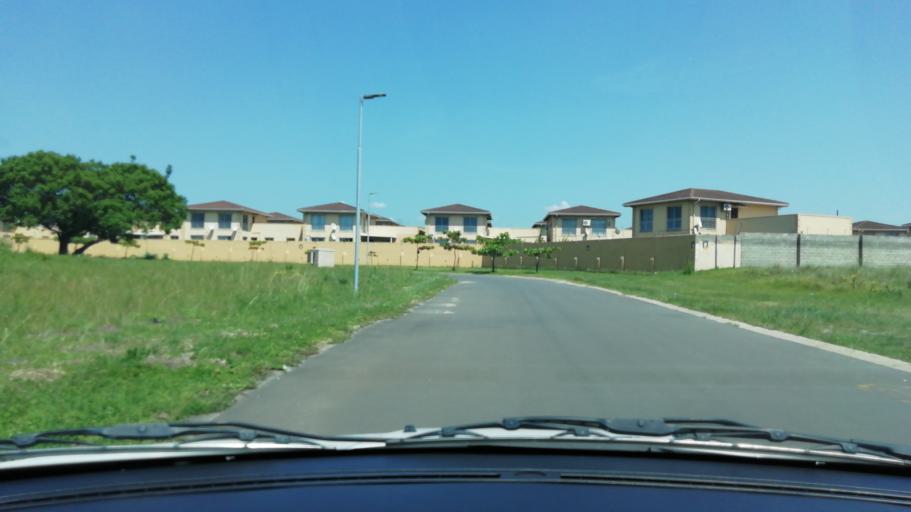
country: ZA
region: KwaZulu-Natal
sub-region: uThungulu District Municipality
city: Richards Bay
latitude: -28.7405
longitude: 32.0516
